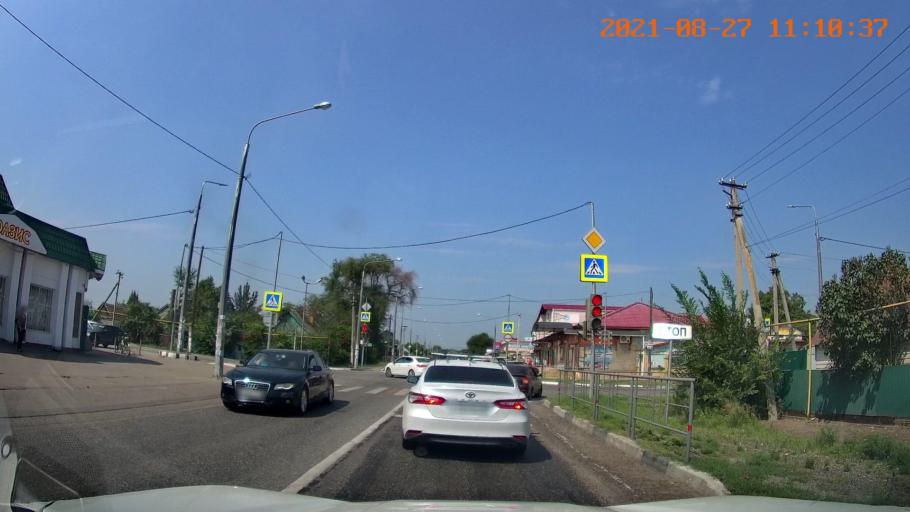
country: RU
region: Stavropol'skiy
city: Ivanovskoye
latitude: 44.5716
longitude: 41.8718
